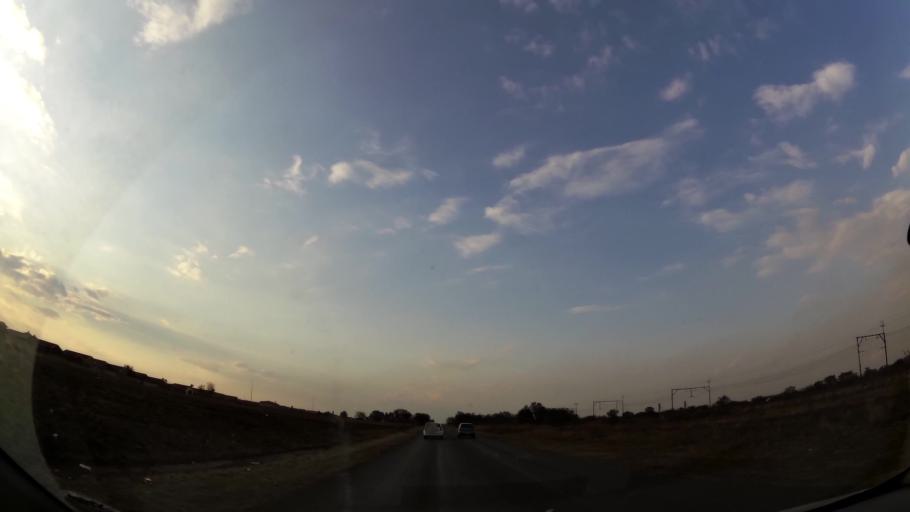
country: ZA
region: Gauteng
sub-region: City of Johannesburg Metropolitan Municipality
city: Orange Farm
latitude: -26.5813
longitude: 27.8559
